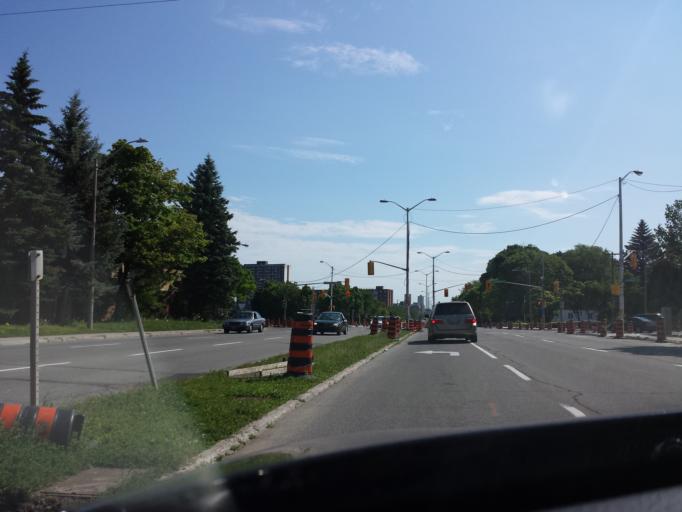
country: CA
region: Ontario
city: Bells Corners
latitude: 45.3603
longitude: -75.7930
